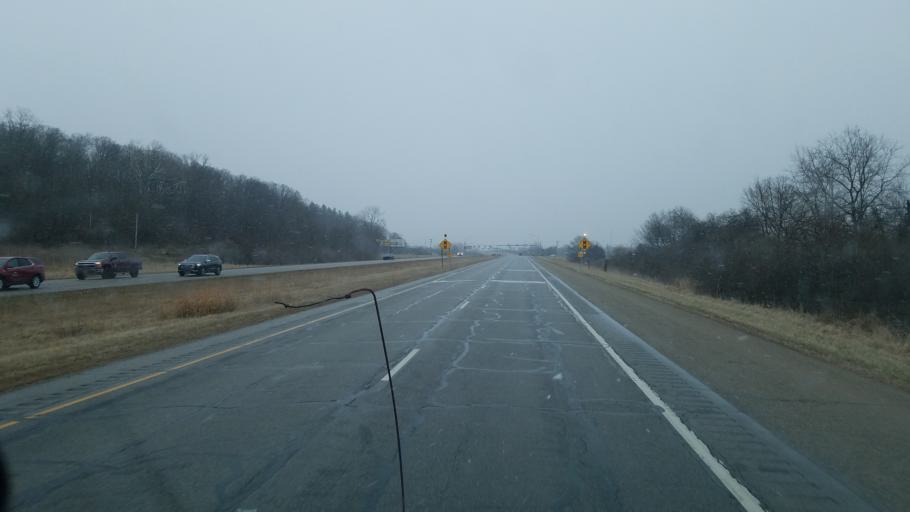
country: US
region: Indiana
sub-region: Miami County
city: Peru
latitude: 40.7729
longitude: -86.0882
